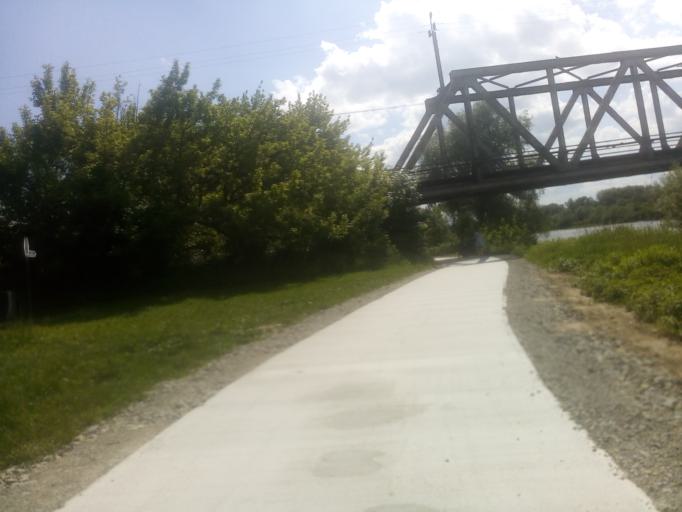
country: PL
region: Lesser Poland Voivodeship
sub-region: Powiat nowosadecki
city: Nowy Sacz
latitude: 49.6244
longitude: 20.6862
